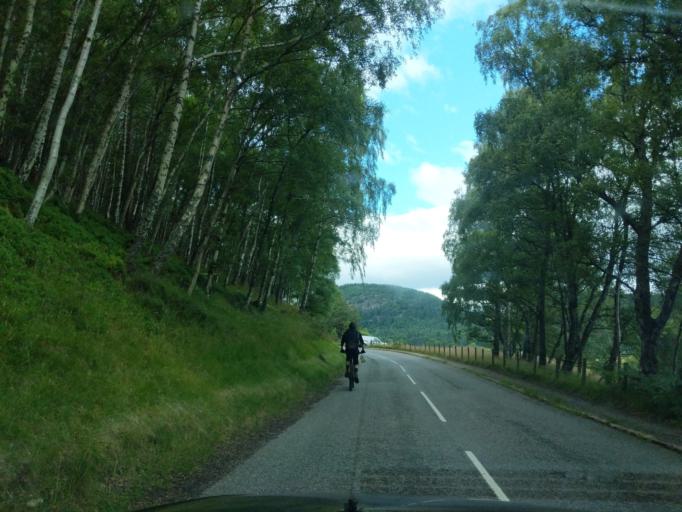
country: GB
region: Scotland
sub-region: Aberdeenshire
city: Ballater
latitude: 57.0551
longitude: -3.0156
